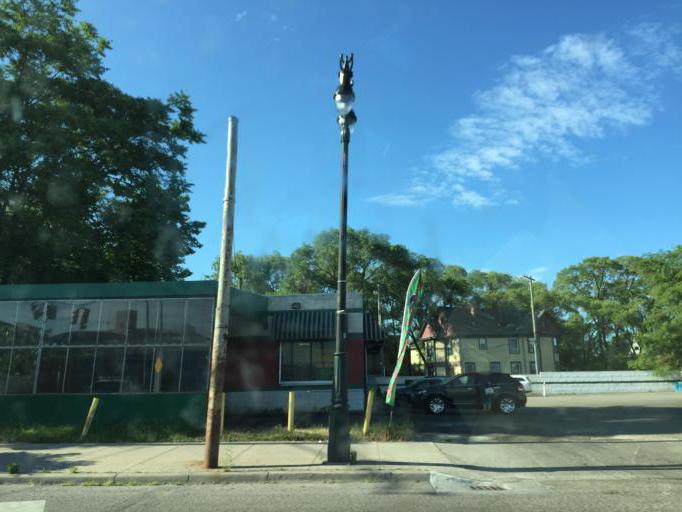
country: US
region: Michigan
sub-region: Wayne County
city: Detroit
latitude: 42.3315
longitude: -83.0627
